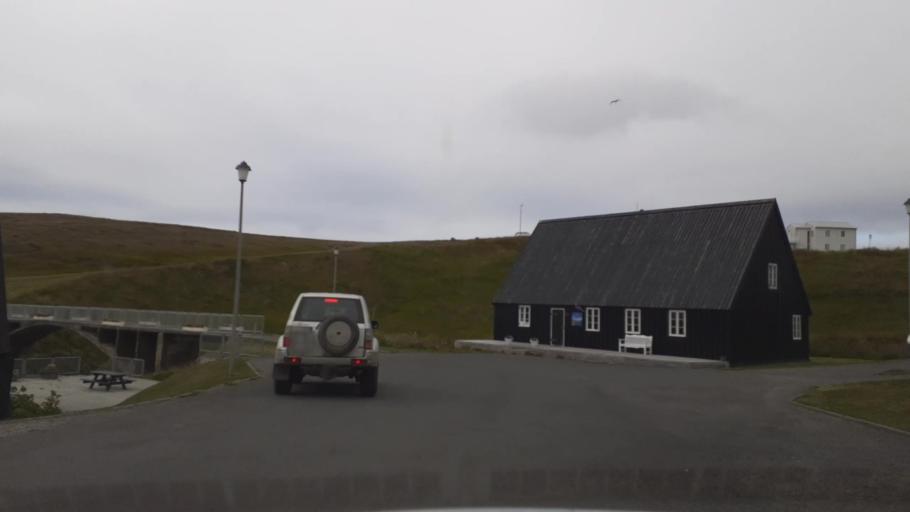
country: IS
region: Northwest
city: Saudarkrokur
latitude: 65.8988
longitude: -19.4167
